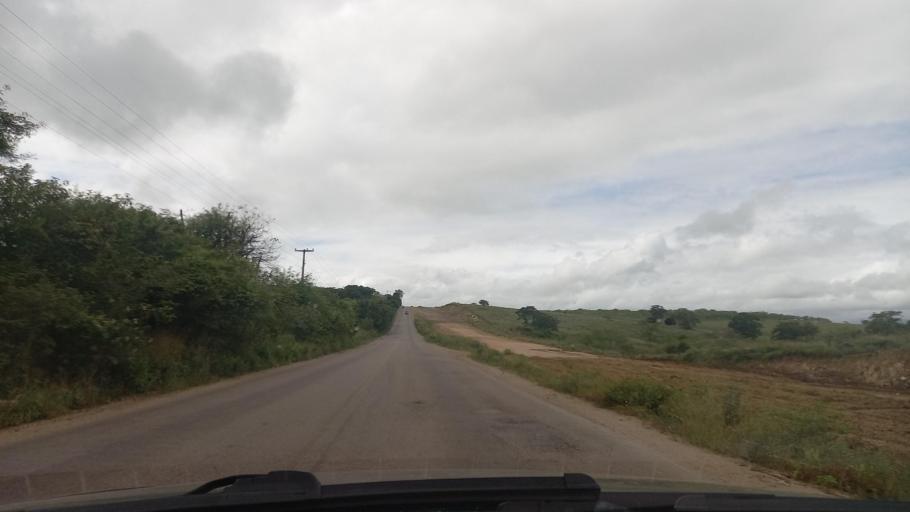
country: BR
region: Alagoas
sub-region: Batalha
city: Batalha
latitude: -9.6419
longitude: -37.1935
